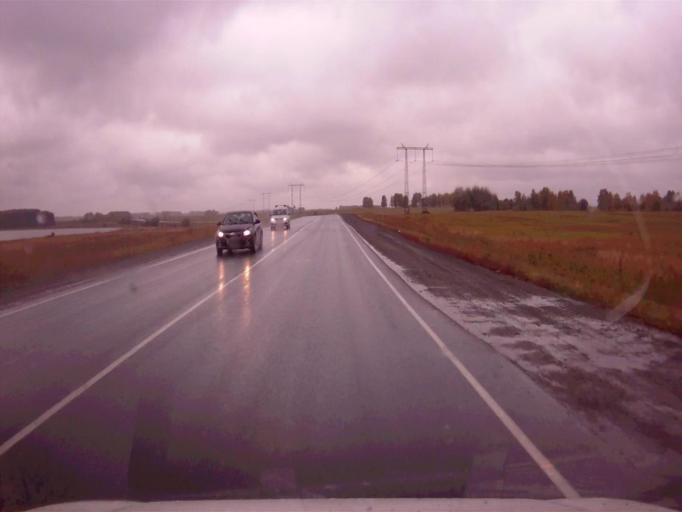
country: RU
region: Chelyabinsk
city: Roshchino
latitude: 55.3898
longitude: 61.1247
